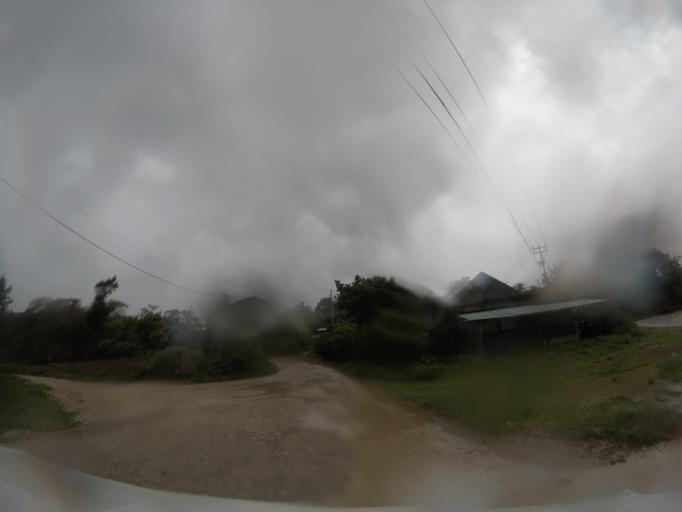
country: TL
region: Baucau
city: Venilale
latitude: -8.6400
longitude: 126.3860
